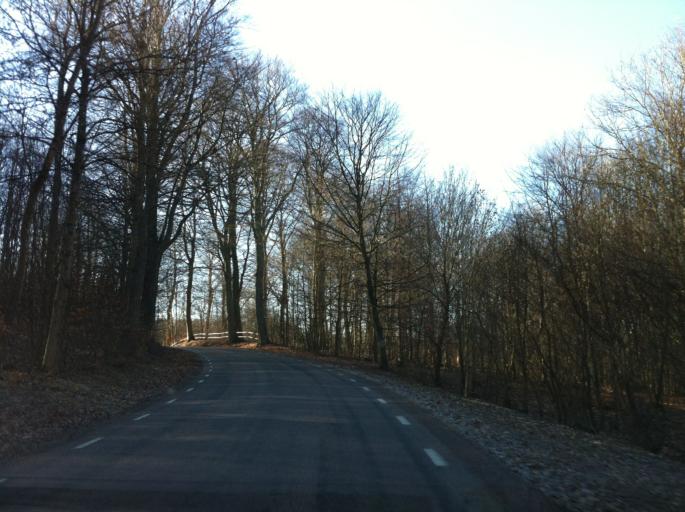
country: SE
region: Skane
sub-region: Svedala Kommun
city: Klagerup
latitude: 55.5697
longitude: 13.2343
